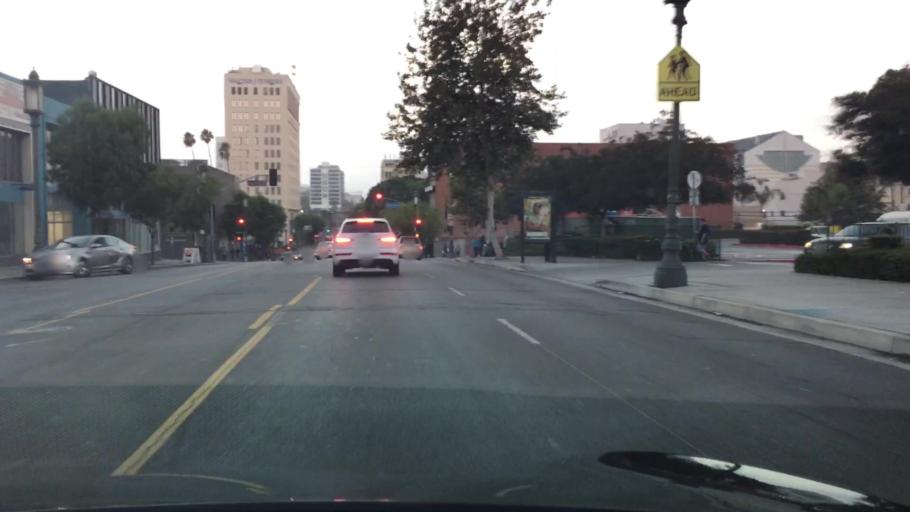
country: US
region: California
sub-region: Los Angeles County
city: Echo Park
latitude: 34.0558
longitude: -118.2716
